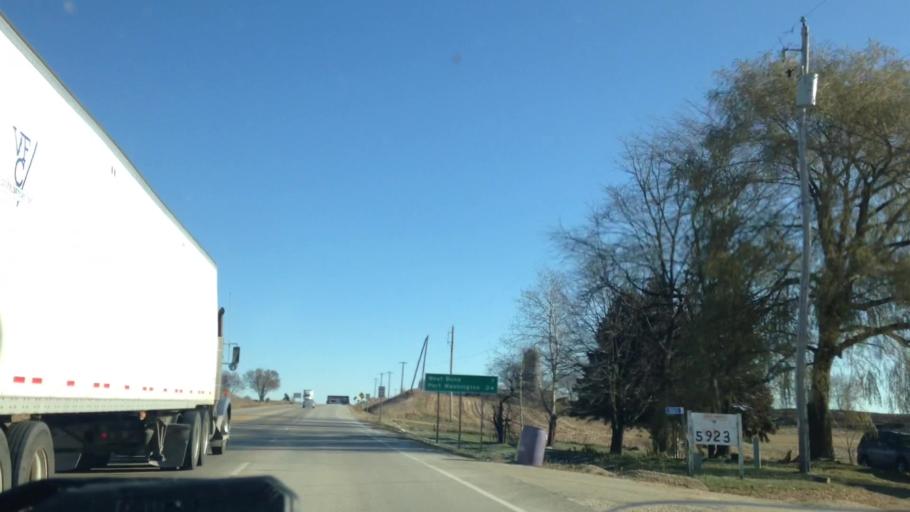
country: US
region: Wisconsin
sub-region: Washington County
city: Slinger
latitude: 43.4250
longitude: -88.3327
